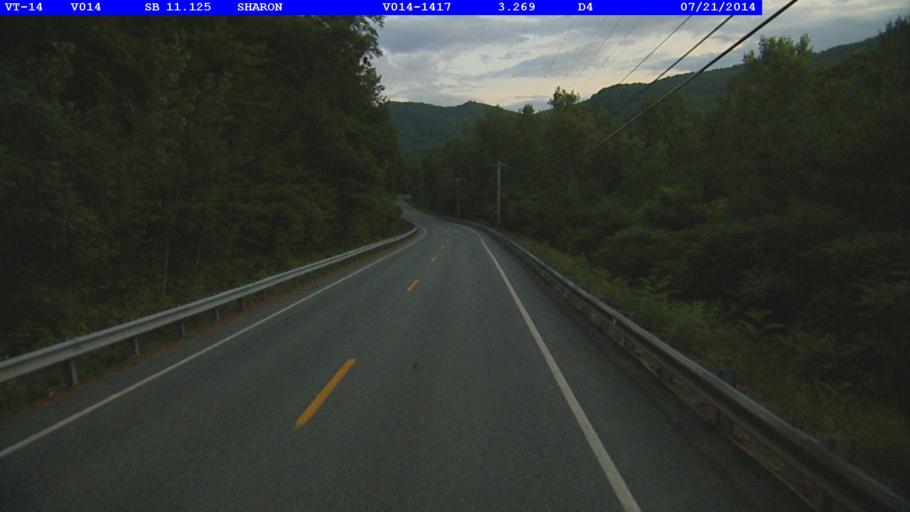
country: US
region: Vermont
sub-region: Windsor County
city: Woodstock
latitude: 43.7632
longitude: -72.4485
